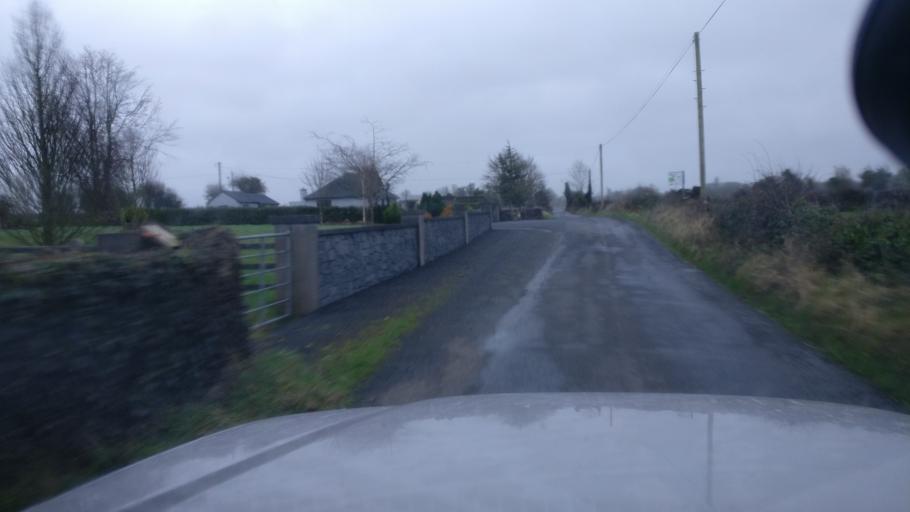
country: IE
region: Connaught
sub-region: County Galway
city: Loughrea
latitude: 53.2312
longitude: -8.6015
